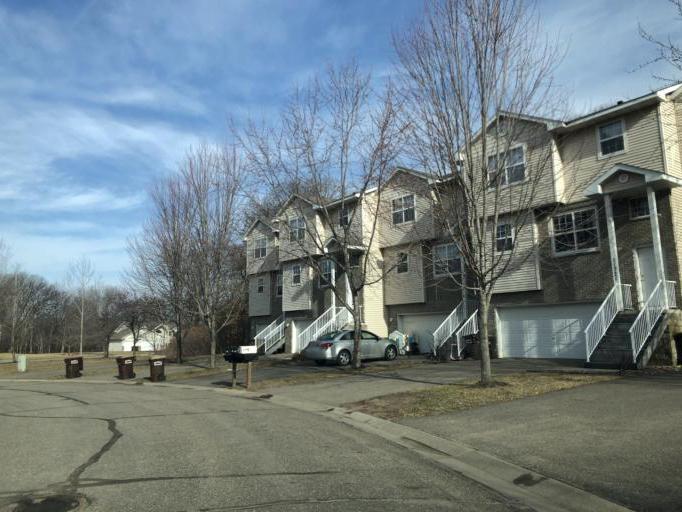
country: US
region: Minnesota
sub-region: Sherburne County
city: Becker
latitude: 45.4005
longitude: -93.8525
